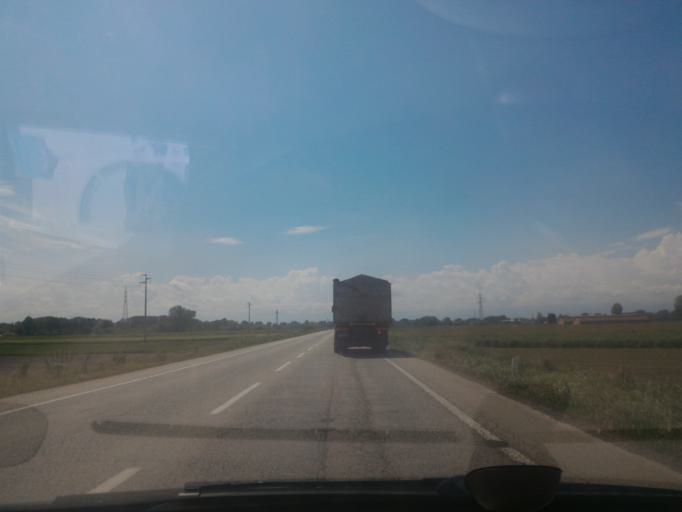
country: IT
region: Piedmont
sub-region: Provincia di Torino
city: Villastellone
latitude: 44.9154
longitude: 7.7090
